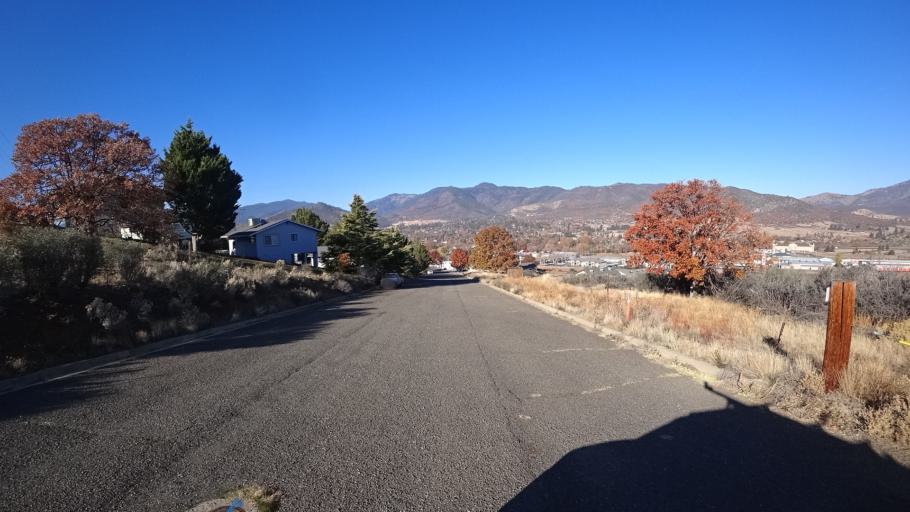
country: US
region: California
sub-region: Siskiyou County
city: Yreka
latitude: 41.7323
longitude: -122.6218
